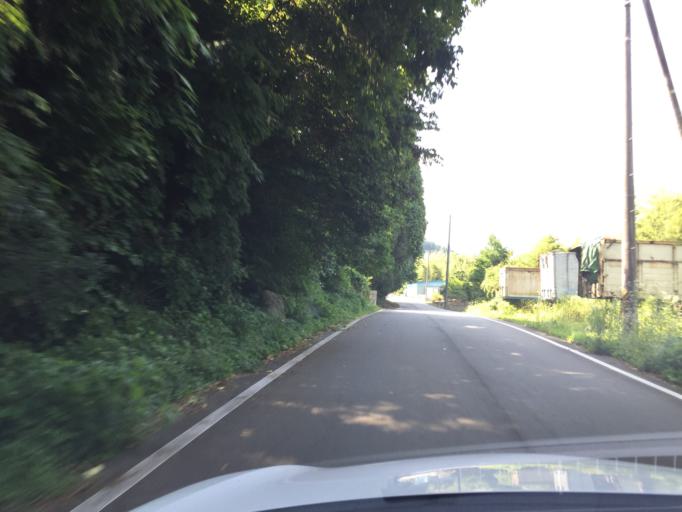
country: JP
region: Ibaraki
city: Kitaibaraki
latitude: 36.9304
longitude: 140.7341
